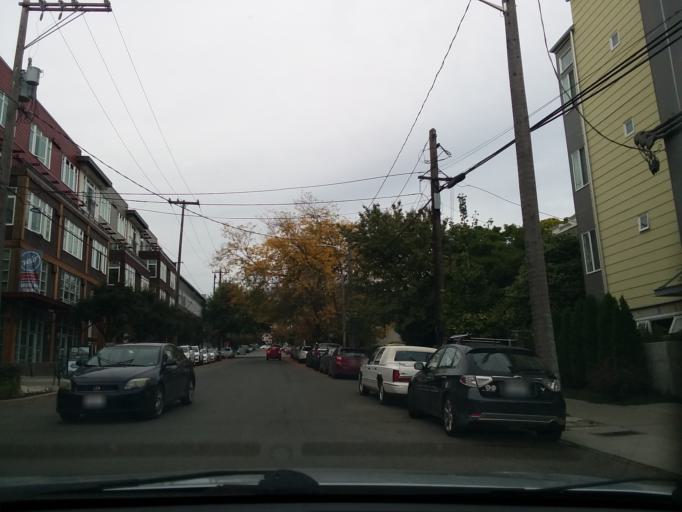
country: US
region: Washington
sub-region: King County
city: Seattle
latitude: 47.6517
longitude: -122.3440
